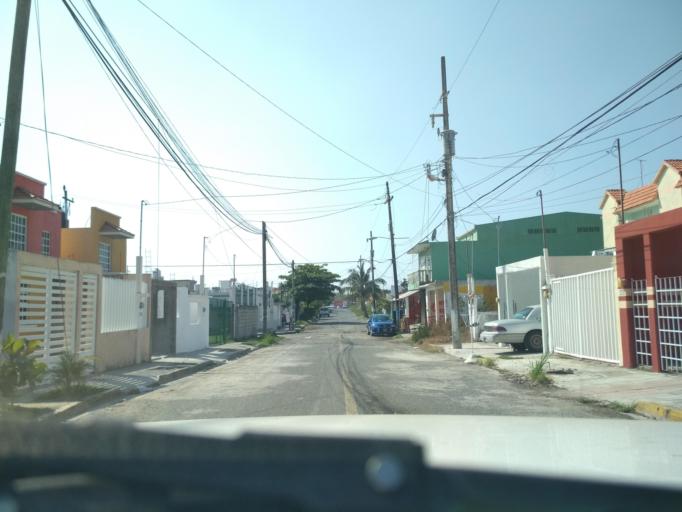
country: MX
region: Veracruz
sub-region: Veracruz
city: Colonia el Renacimiento
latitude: 19.2185
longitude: -96.2131
